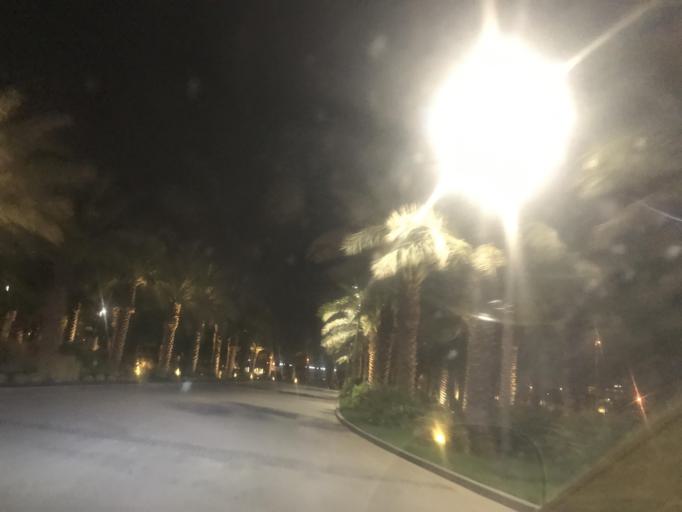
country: SA
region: Ar Riyad
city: Riyadh
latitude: 24.8419
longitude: 46.7323
